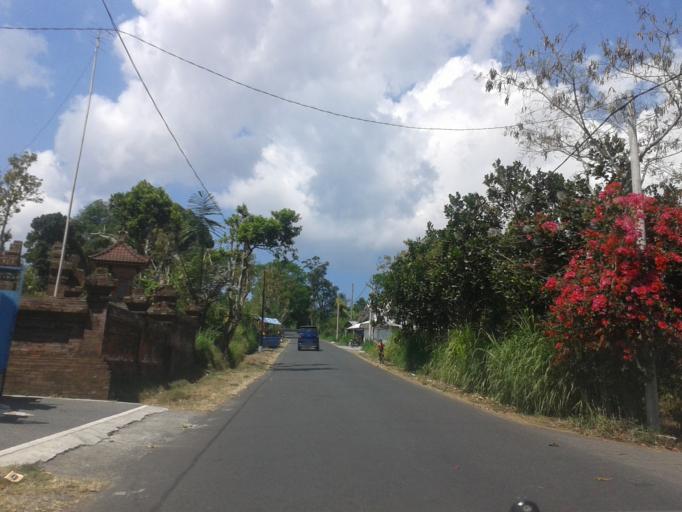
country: ID
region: Bali
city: Banjar Kedisan
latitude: -8.2903
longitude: 115.3426
